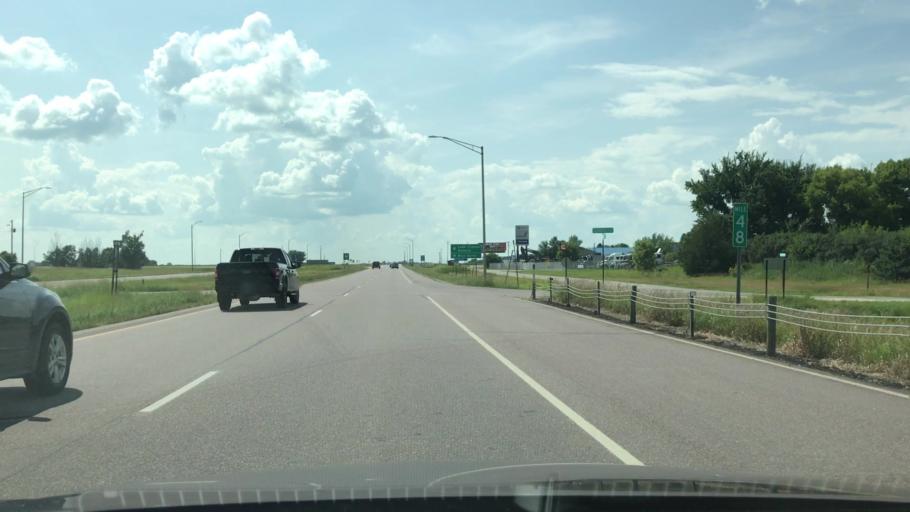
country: US
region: Minnesota
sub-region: Nicollet County
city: North Mankato
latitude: 44.1446
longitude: -94.1125
